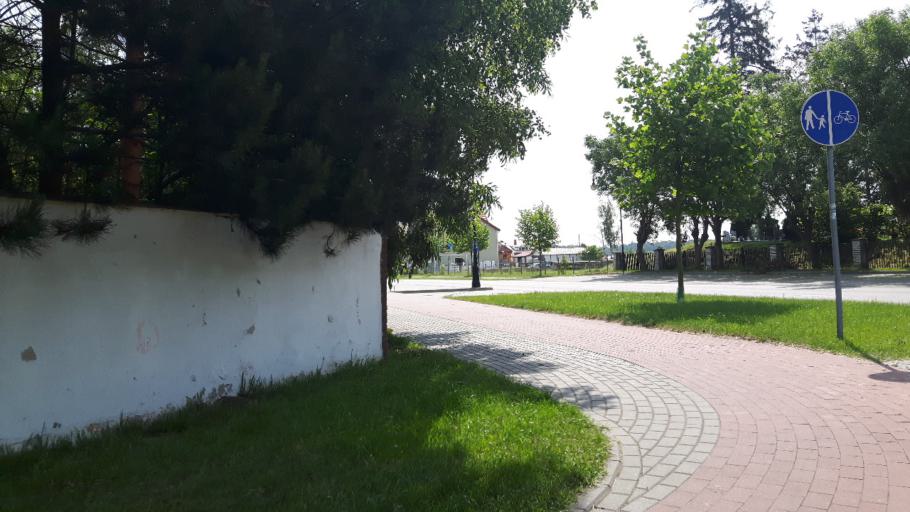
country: PL
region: Pomeranian Voivodeship
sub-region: Powiat leborski
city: Leba
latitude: 54.7506
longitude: 17.5631
